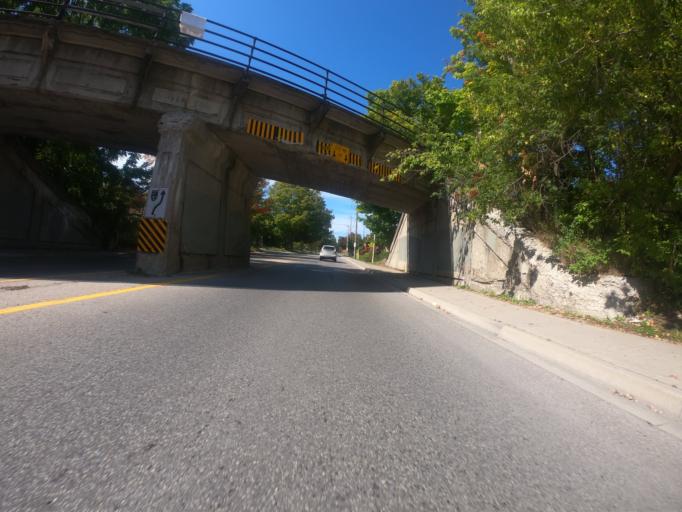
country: CA
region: Ontario
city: Waterloo
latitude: 43.4494
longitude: -80.5043
